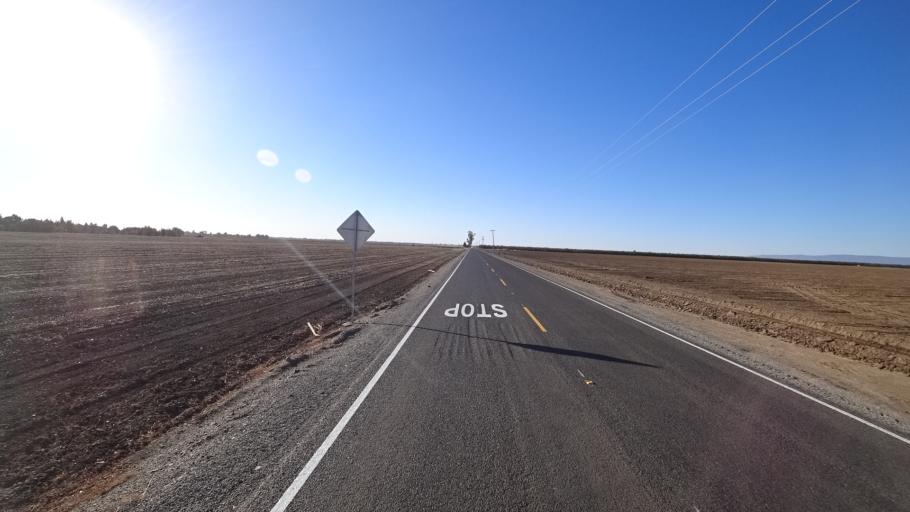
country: US
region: California
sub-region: Yolo County
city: Davis
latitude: 38.5891
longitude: -121.7856
